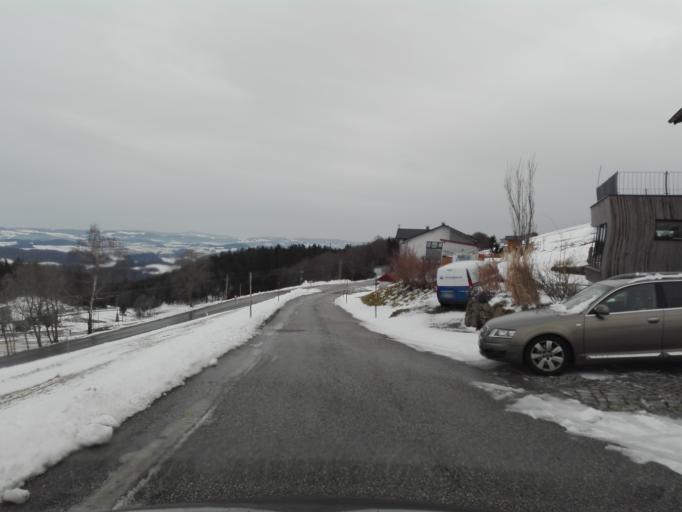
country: AT
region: Upper Austria
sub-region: Politischer Bezirk Rohrbach
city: Pfarrkirchen im Muehlkreis
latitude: 48.5585
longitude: 13.8377
